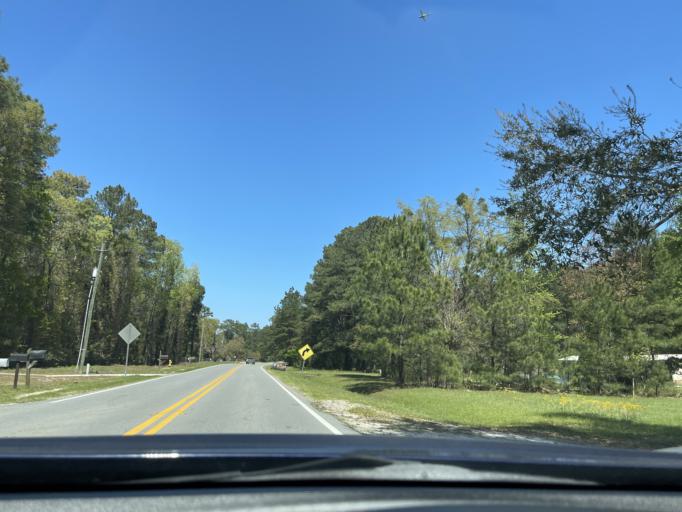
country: US
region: Georgia
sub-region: Chatham County
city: Pooler
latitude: 32.0929
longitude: -81.2405
